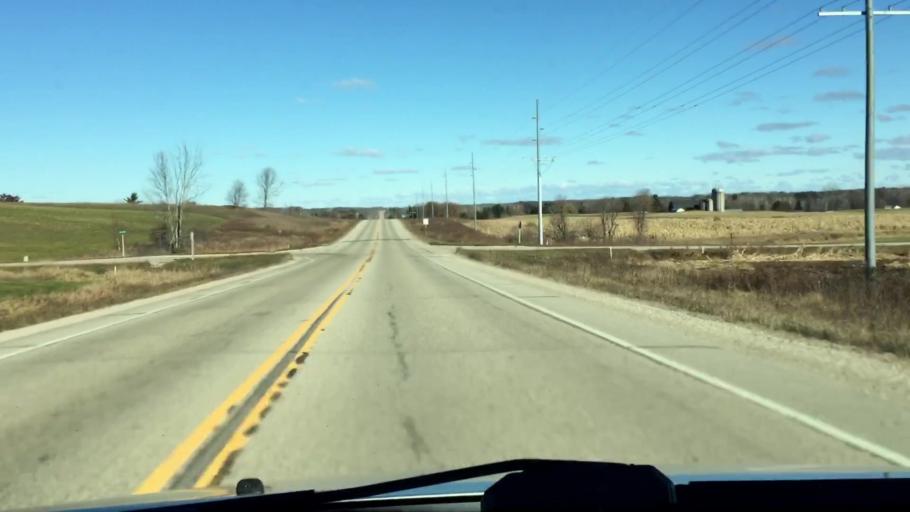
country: US
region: Wisconsin
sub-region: Oconto County
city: Gillett
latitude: 44.8665
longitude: -88.2476
